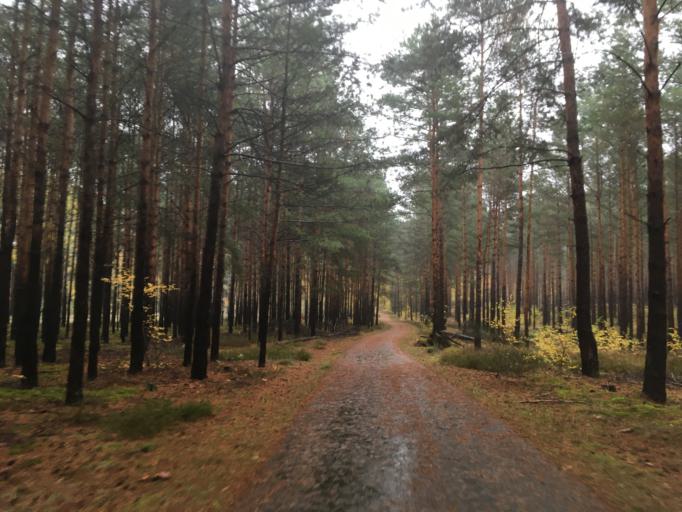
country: DE
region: Brandenburg
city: Halbe
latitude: 52.0316
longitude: 13.7767
